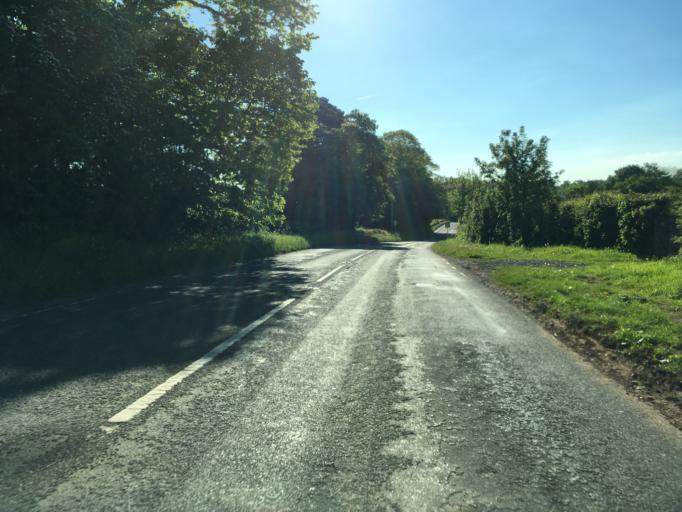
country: GB
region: England
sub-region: North Somerset
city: Easton-in-Gordano
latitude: 51.4450
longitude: -2.7024
